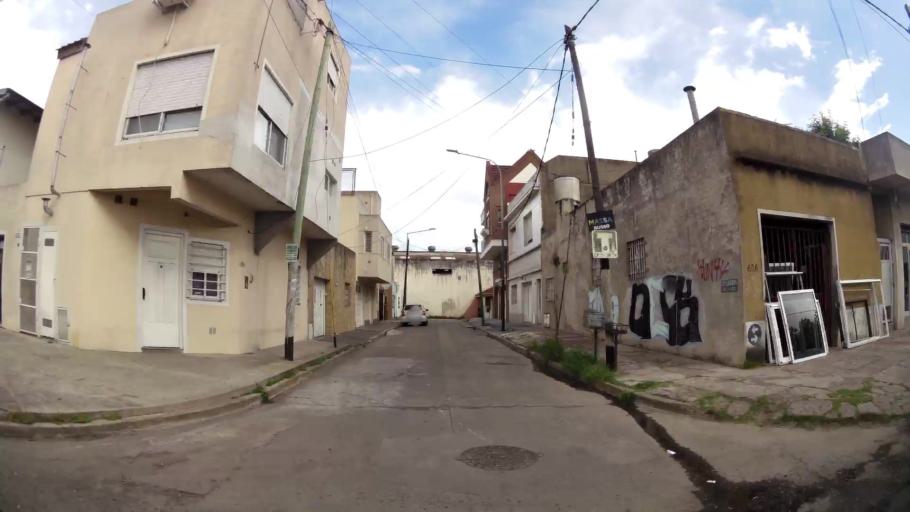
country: AR
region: Buenos Aires
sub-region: Partido de Lanus
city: Lanus
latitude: -34.6970
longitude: -58.3775
